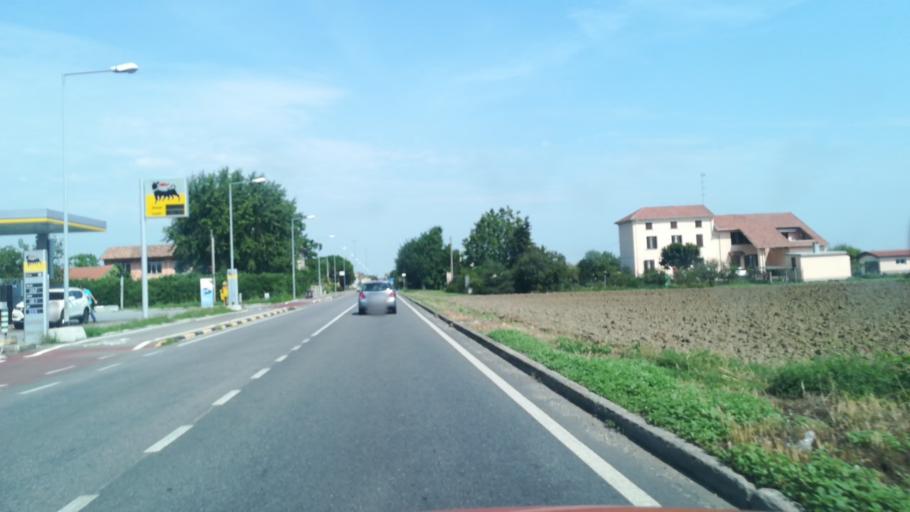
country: IT
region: Piedmont
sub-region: Provincia di Alessandria
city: Casale Monferrato
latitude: 45.1107
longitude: 8.4517
